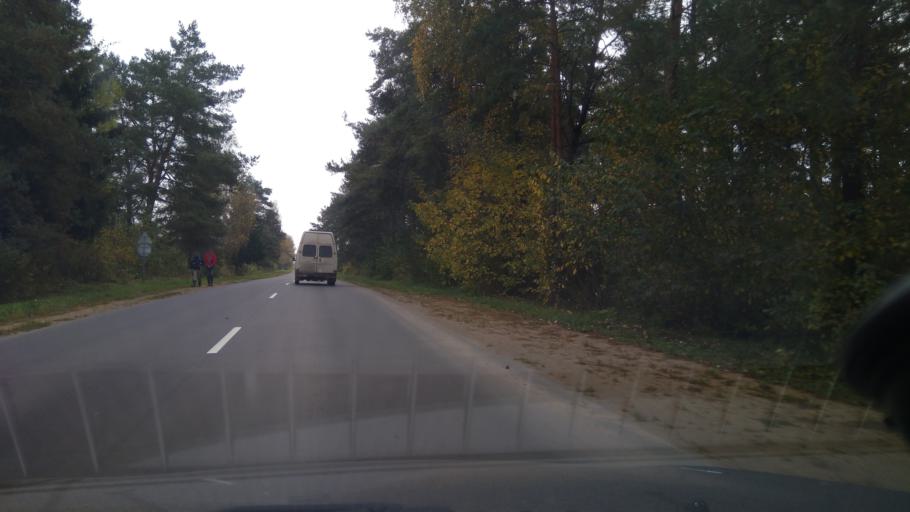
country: BY
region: Minsk
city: Rudzyensk
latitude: 53.6120
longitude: 27.7949
